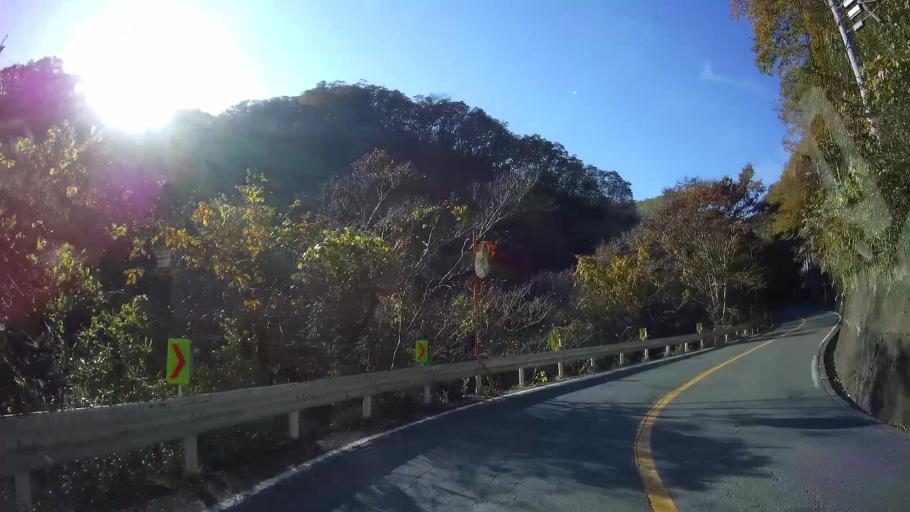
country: JP
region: Yamanashi
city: Uenohara
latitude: 35.6043
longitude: 139.1243
